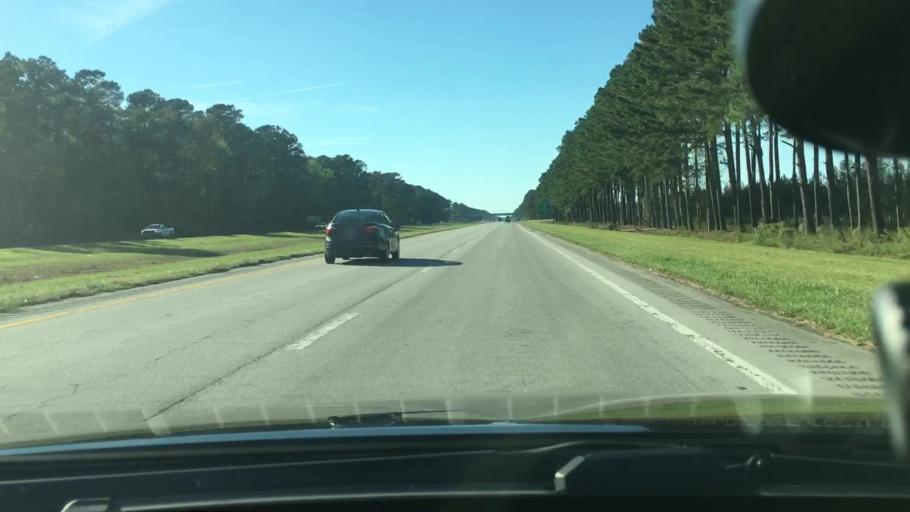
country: US
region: North Carolina
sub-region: Craven County
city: Trent Woods
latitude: 35.1238
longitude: -77.1229
